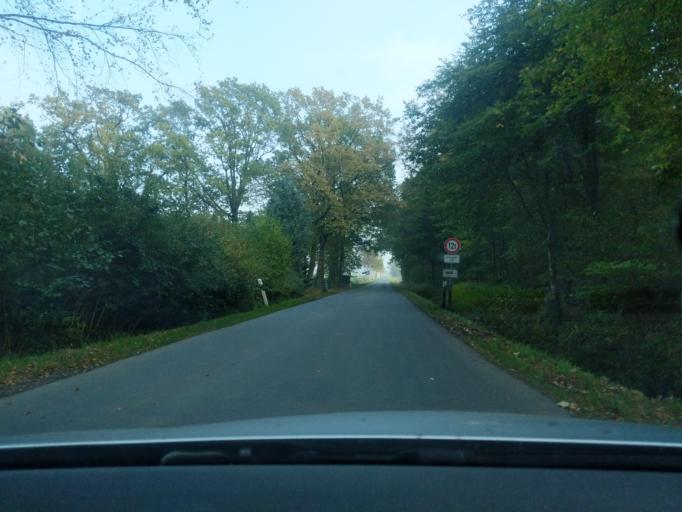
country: DE
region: Lower Saxony
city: Wanna
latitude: 53.7257
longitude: 8.7927
